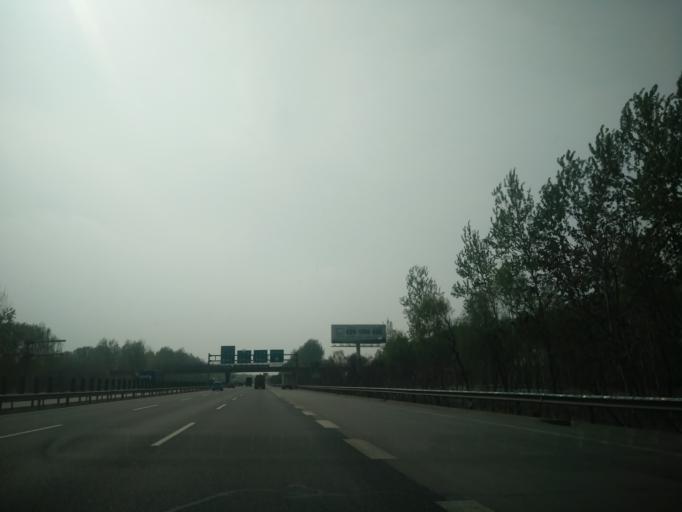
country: CN
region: Beijing
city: Xiji
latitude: 39.8023
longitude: 116.8278
